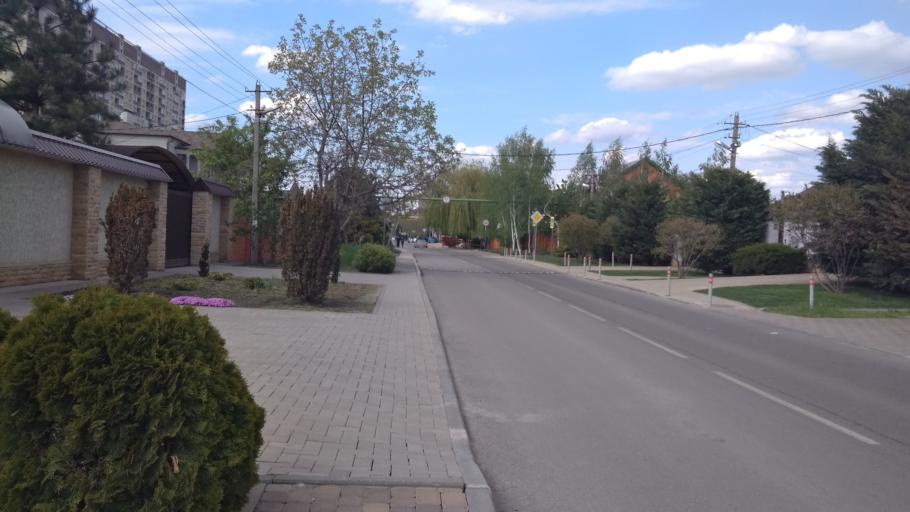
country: RU
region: Krasnodarskiy
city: Krasnodar
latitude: 45.0759
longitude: 39.0048
